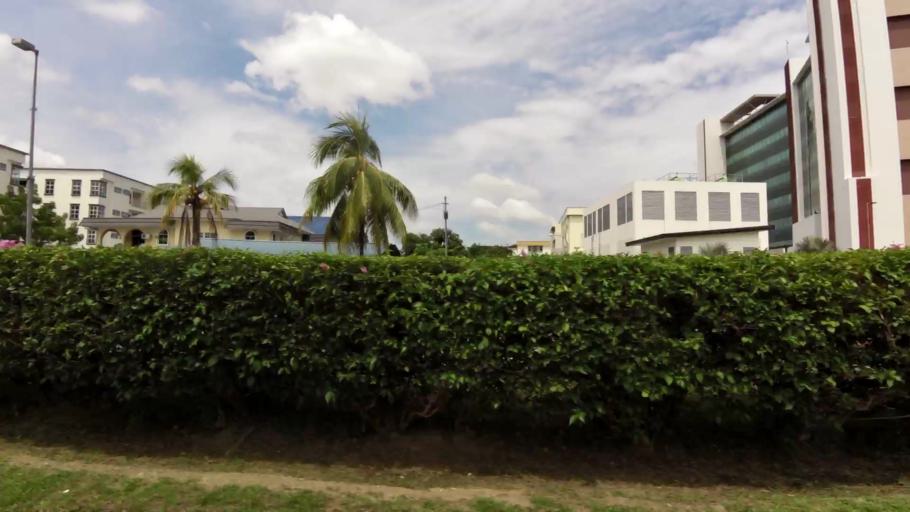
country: BN
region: Brunei and Muara
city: Bandar Seri Begawan
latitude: 4.9383
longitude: 114.9409
